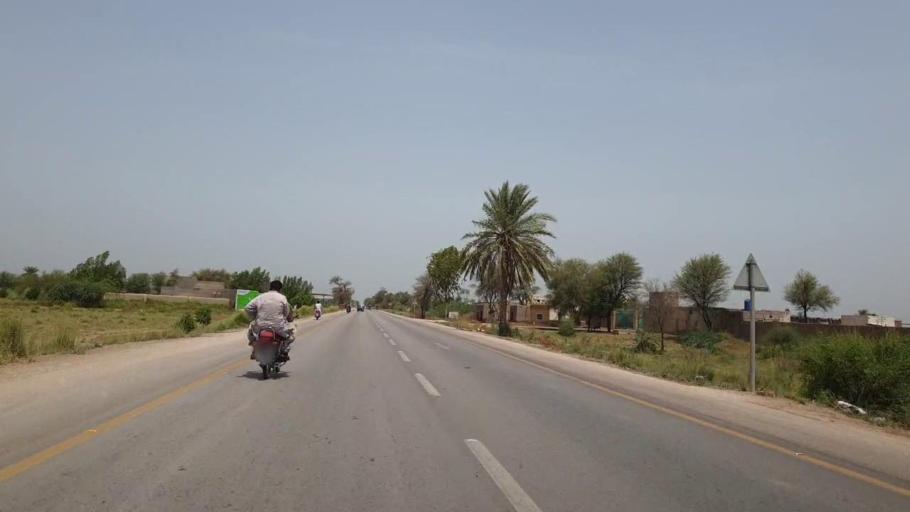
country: PK
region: Sindh
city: Nawabshah
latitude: 26.2156
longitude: 68.5073
